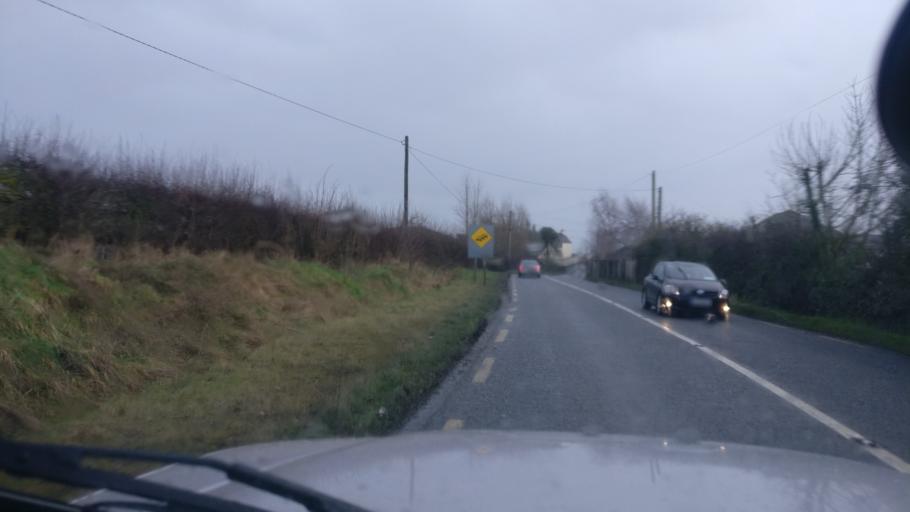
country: IE
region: Leinster
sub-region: Kilkenny
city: Kilkenny
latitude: 52.7095
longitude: -7.2792
